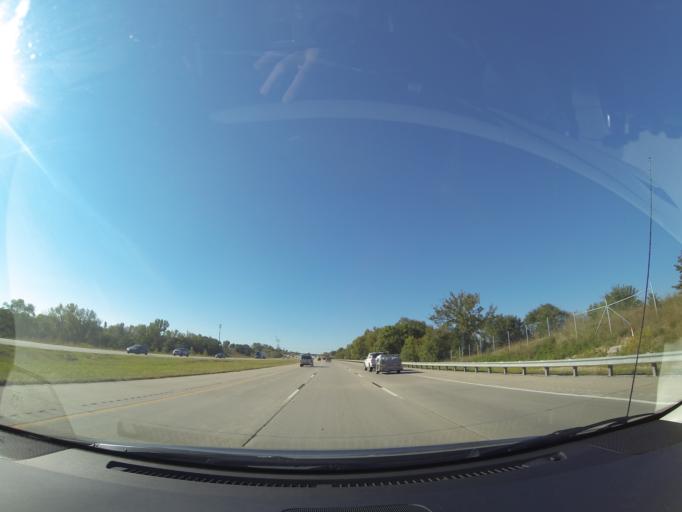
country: US
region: Nebraska
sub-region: Saunders County
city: Ashland
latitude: 41.0213
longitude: -96.3022
